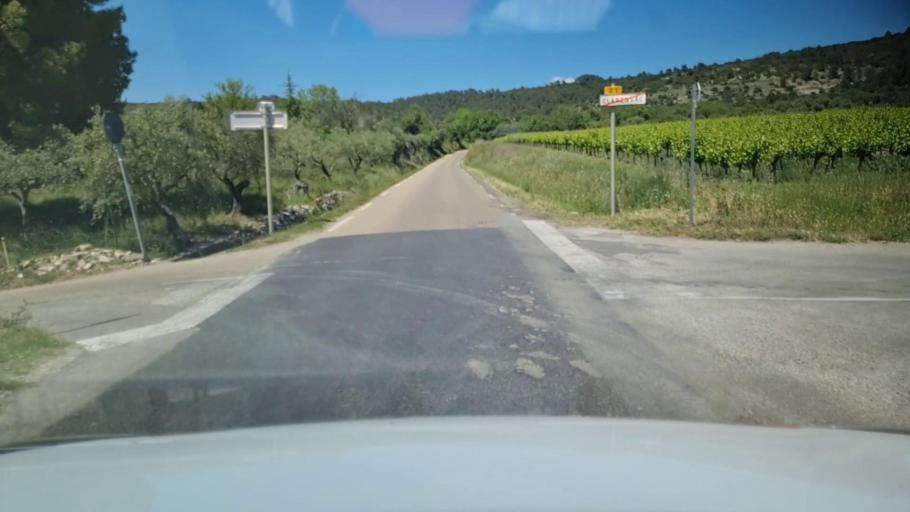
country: FR
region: Languedoc-Roussillon
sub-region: Departement du Gard
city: Clarensac
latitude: 43.8305
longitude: 4.2168
